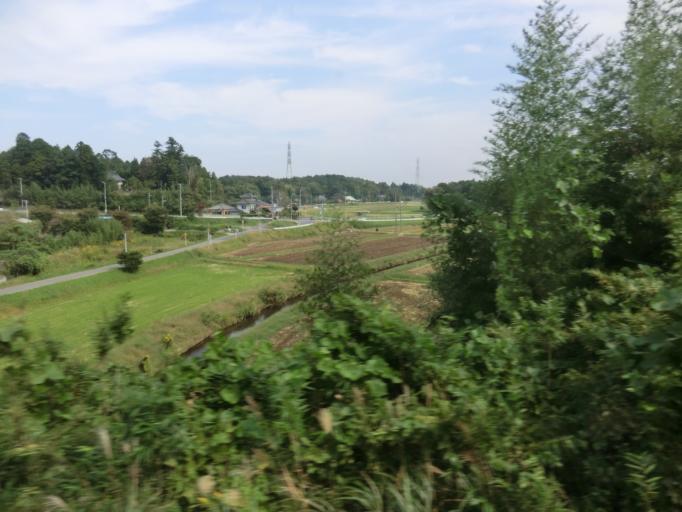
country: JP
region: Chiba
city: Shisui
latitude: 35.7000
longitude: 140.2742
